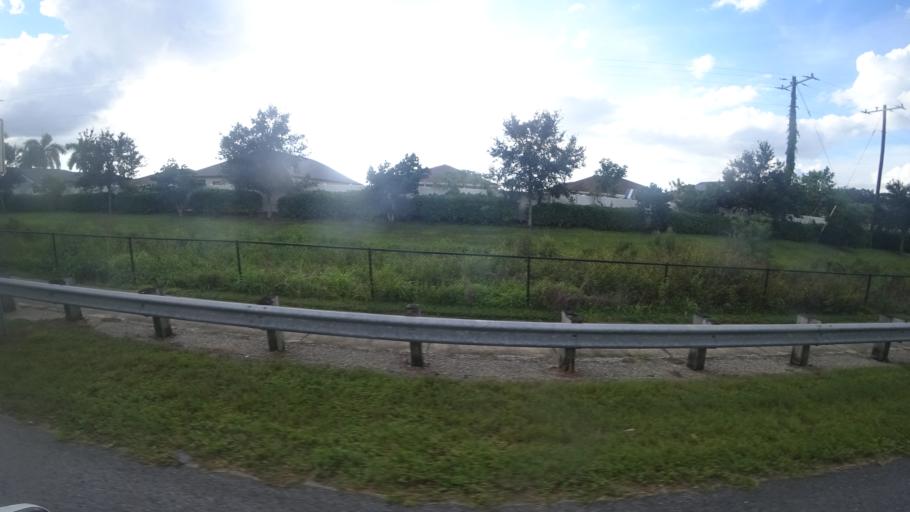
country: US
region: Florida
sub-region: Manatee County
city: Memphis
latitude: 27.5347
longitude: -82.5482
